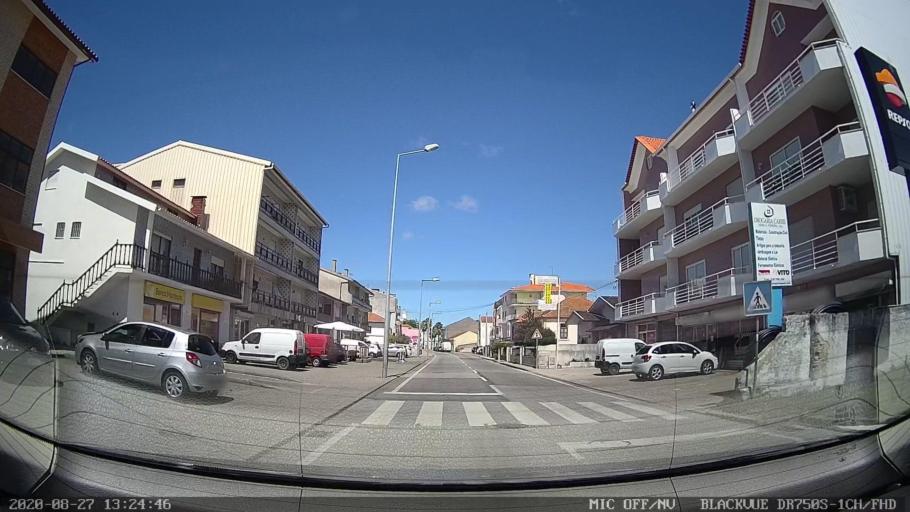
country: PT
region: Aveiro
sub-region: Vagos
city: Vagos
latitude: 40.5514
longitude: -8.6801
